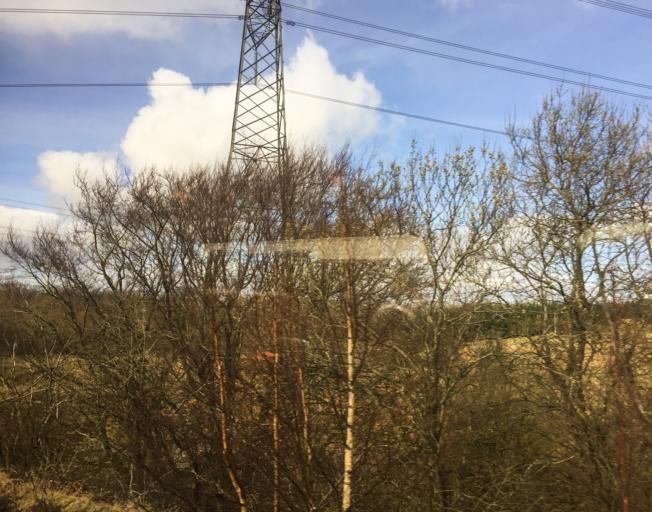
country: GB
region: Scotland
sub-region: North Lanarkshire
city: Glenboig
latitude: 55.8827
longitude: -4.0608
